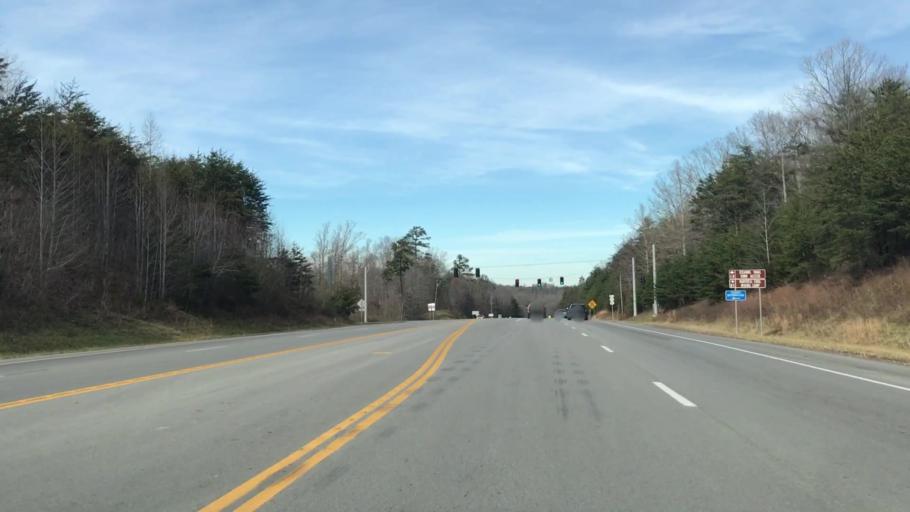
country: US
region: Kentucky
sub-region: McCreary County
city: Stearns
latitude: 36.7029
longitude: -84.4599
